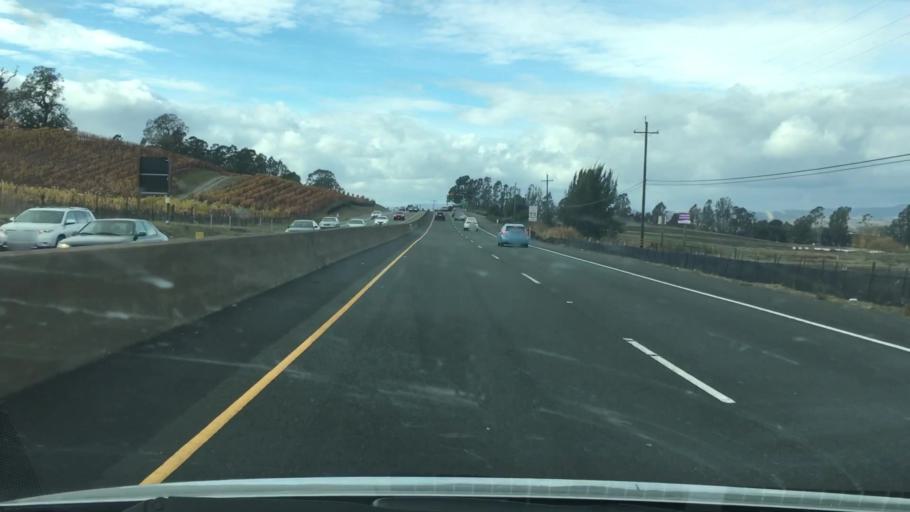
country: US
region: California
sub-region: Napa County
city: American Canyon
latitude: 38.2225
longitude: -122.2482
